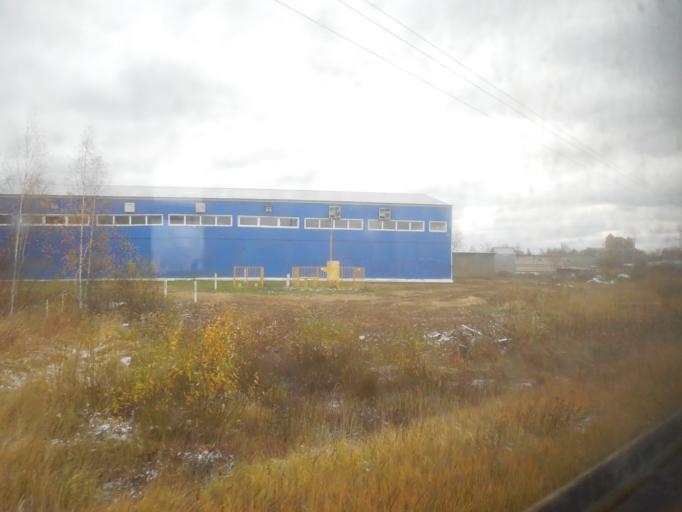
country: RU
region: Moskovskaya
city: Bol'shiye Vyazemy
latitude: 55.6177
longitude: 36.9725
